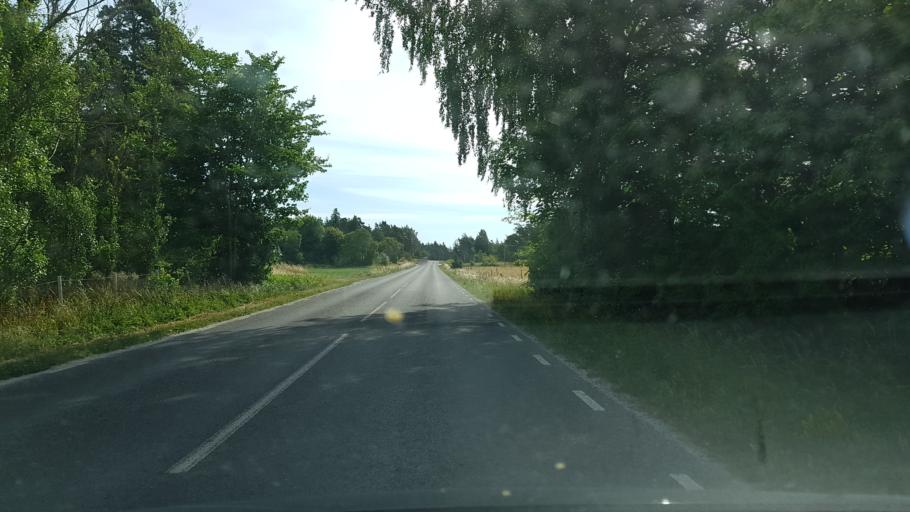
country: SE
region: Gotland
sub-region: Gotland
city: Hemse
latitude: 57.4332
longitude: 18.6072
